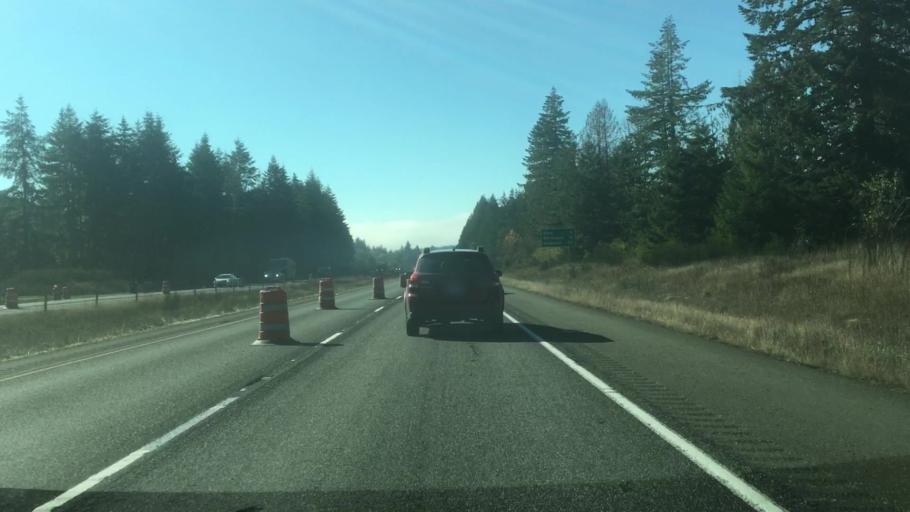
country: US
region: Washington
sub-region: Grays Harbor County
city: McCleary
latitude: 47.0530
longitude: -123.2923
